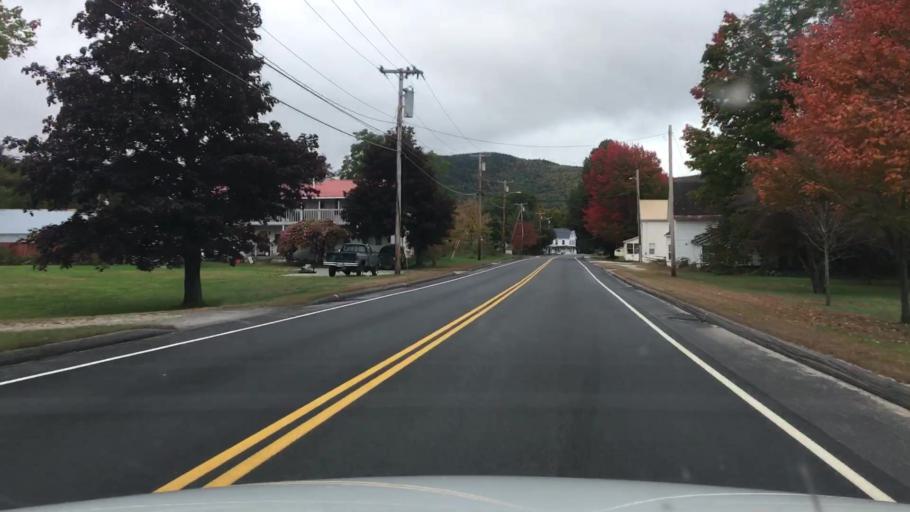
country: US
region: Maine
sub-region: Oxford County
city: Bethel
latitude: 44.4041
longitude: -70.8584
